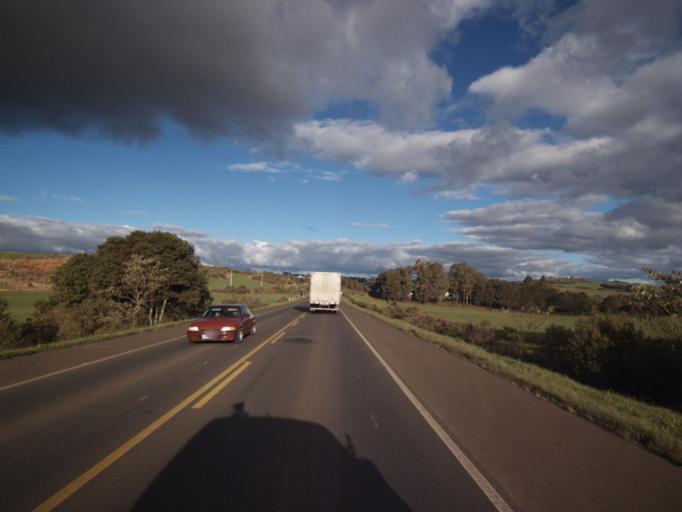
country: BR
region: Santa Catarina
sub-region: Campos Novos
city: Campos Novos
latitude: -27.3770
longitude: -51.2446
